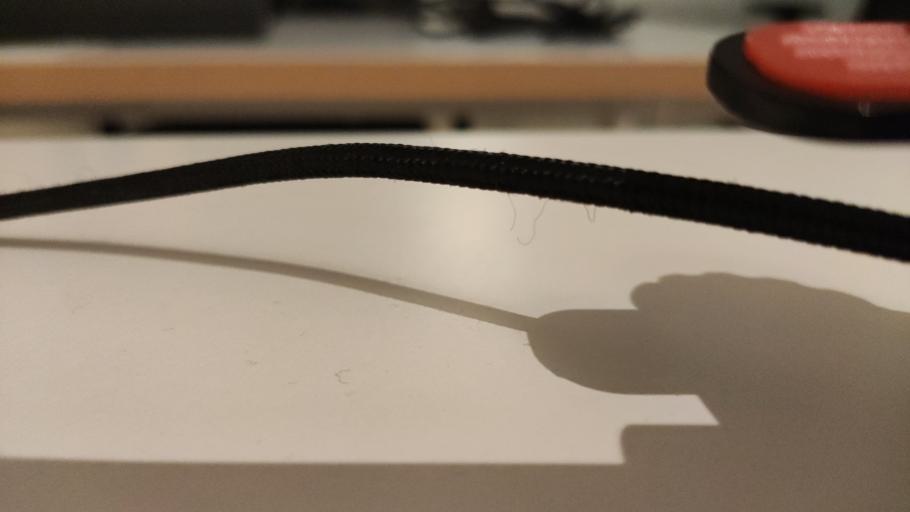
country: RU
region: Moskovskaya
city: Il'inskiy Pogost
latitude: 55.4954
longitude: 38.8745
